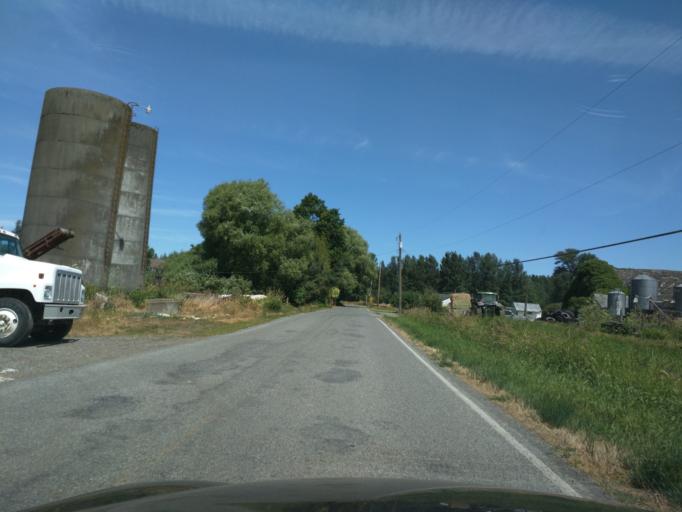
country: US
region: Washington
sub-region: Whatcom County
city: Everson
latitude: 48.9247
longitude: -122.3974
